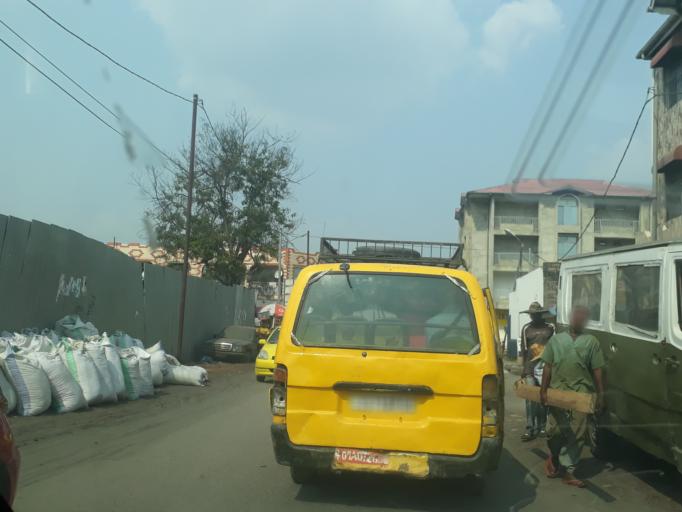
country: CD
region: Kinshasa
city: Kinshasa
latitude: -4.3243
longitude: 15.3161
